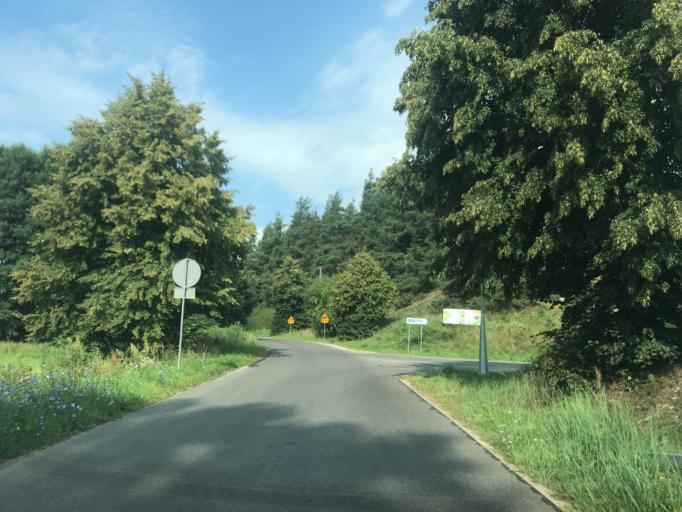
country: PL
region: Warmian-Masurian Voivodeship
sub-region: Powiat nowomiejski
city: Kurzetnik
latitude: 53.3705
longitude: 19.5402
